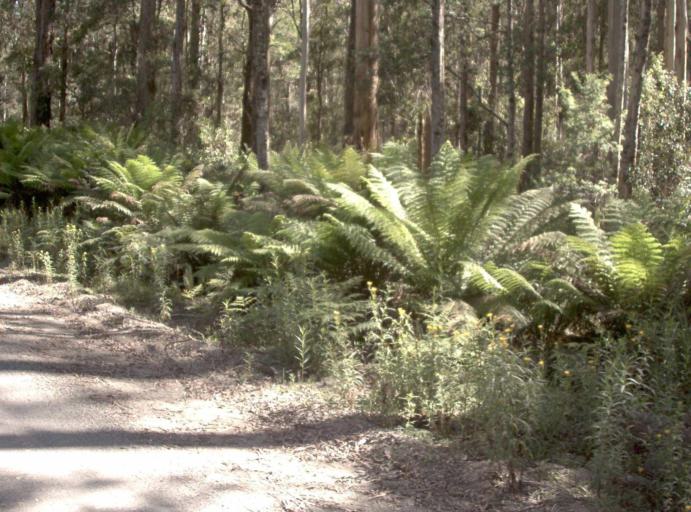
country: AU
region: New South Wales
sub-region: Bombala
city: Bombala
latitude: -37.2410
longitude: 148.7570
